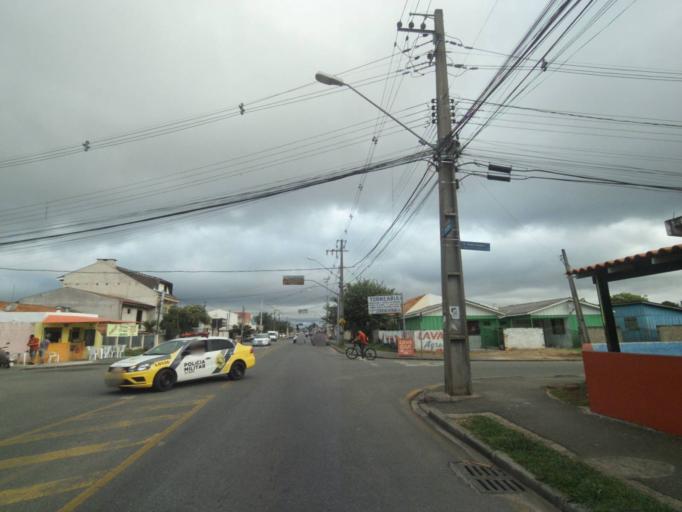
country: BR
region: Parana
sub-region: Pinhais
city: Pinhais
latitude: -25.4573
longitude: -49.2017
